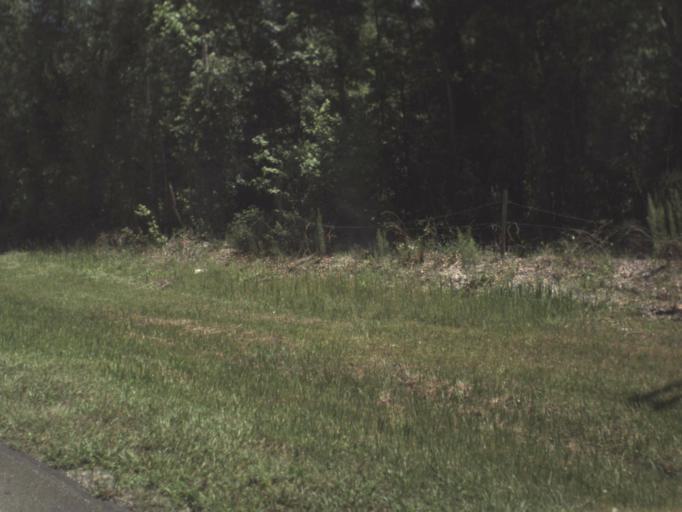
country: US
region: Florida
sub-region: Clay County
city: Keystone Heights
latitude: 29.7520
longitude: -82.0561
